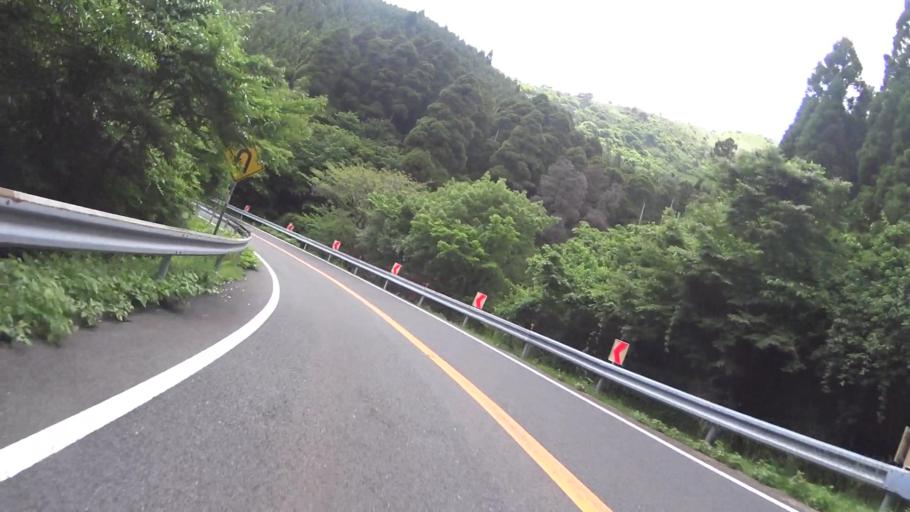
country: JP
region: Kumamoto
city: Aso
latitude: 33.0828
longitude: 131.1897
